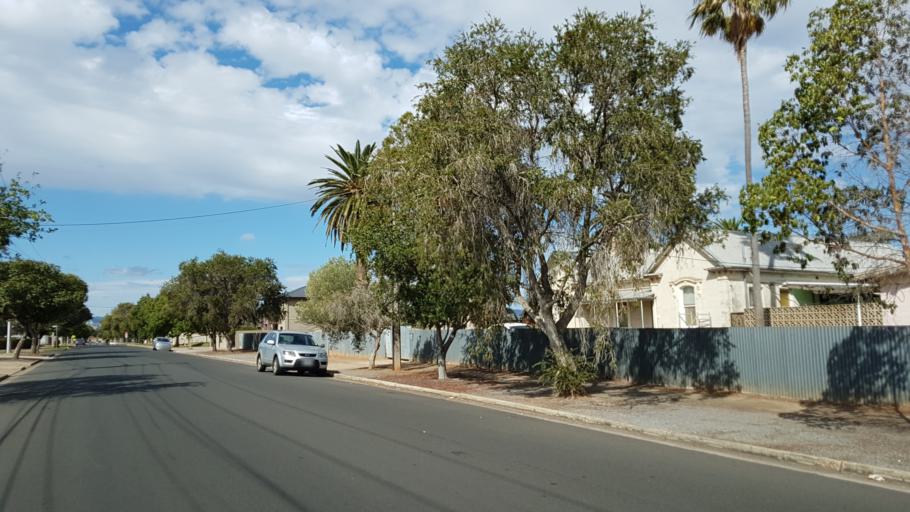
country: AU
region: South Australia
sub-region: City of West Torrens
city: Plympton
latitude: -34.9287
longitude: 138.5465
